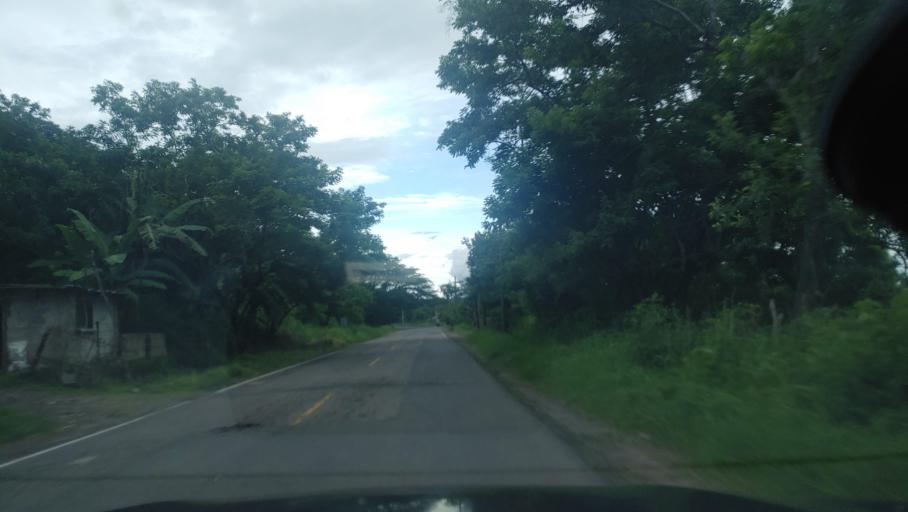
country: HN
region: Choluteca
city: Corpus
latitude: 13.3600
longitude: -86.9870
